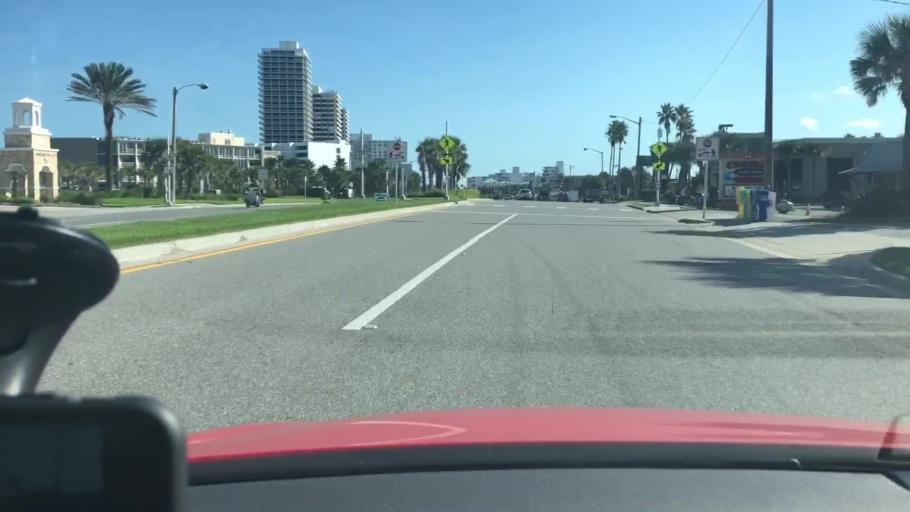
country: US
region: Florida
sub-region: Volusia County
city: Holly Hill
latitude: 29.2716
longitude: -81.0300
